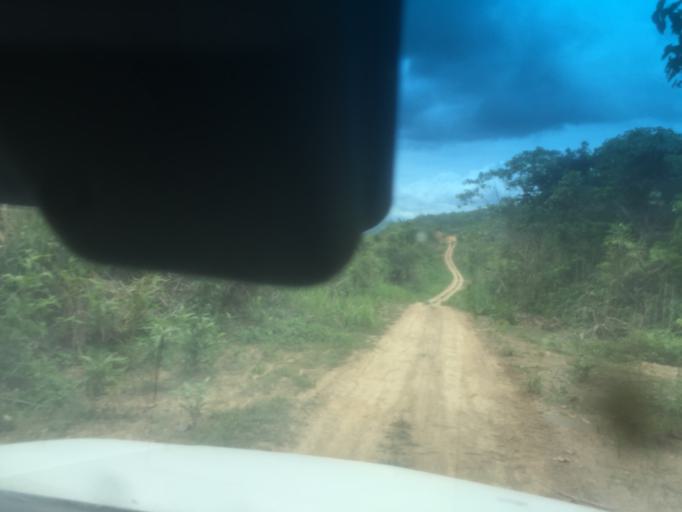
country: LA
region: Phongsali
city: Khoa
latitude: 20.9272
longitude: 102.5396
